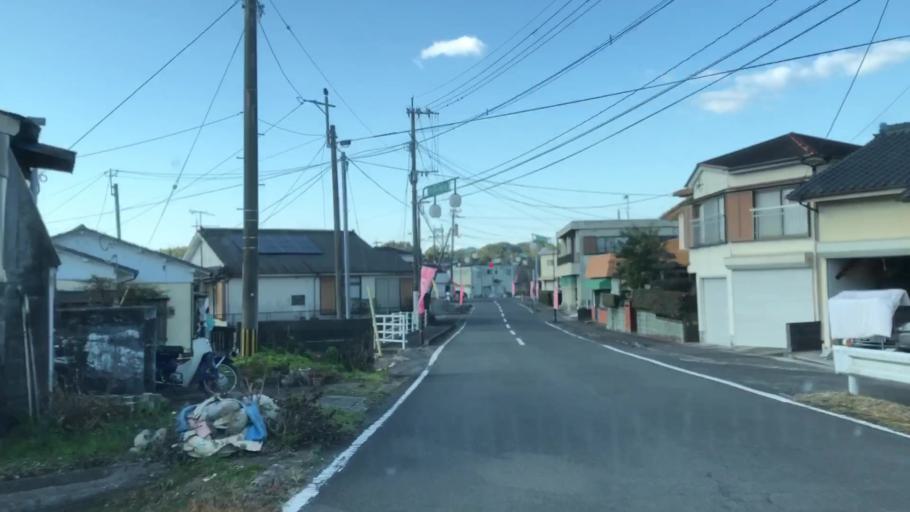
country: JP
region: Kagoshima
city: Satsumasendai
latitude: 31.8622
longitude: 130.3383
